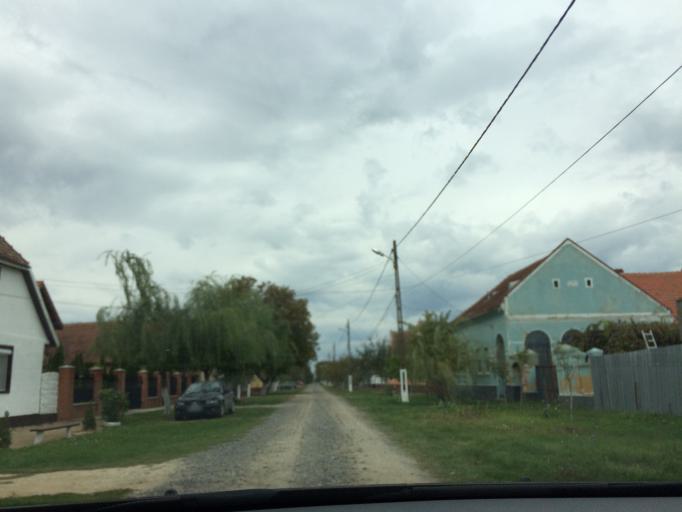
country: RO
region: Timis
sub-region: Comuna Cheveresu Mare
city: Cheveresu Mare
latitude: 45.7280
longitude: 21.4915
